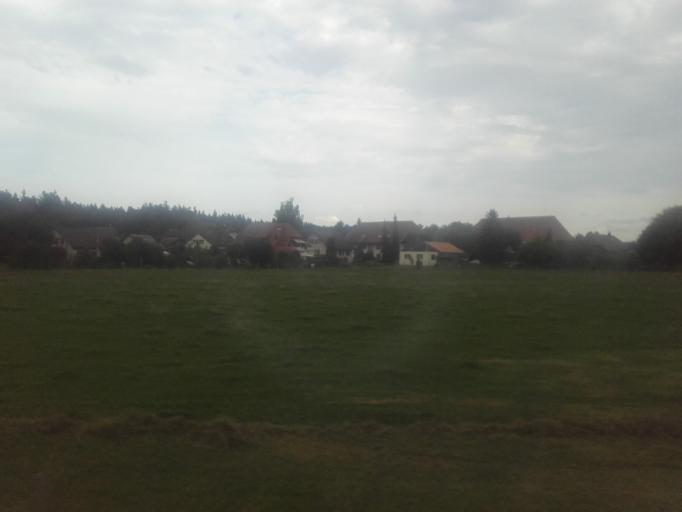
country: CH
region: Bern
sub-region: Emmental District
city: Utzenstorf
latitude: 47.1534
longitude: 7.5565
